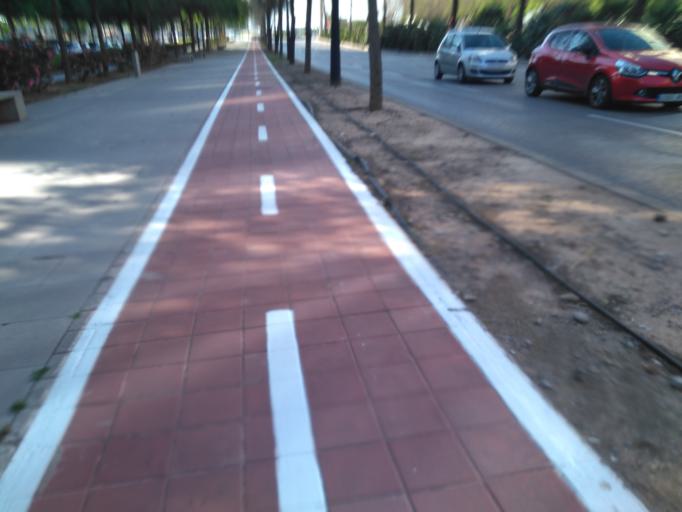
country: ES
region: Valencia
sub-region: Provincia de Valencia
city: Mislata
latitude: 39.4931
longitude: -0.4016
